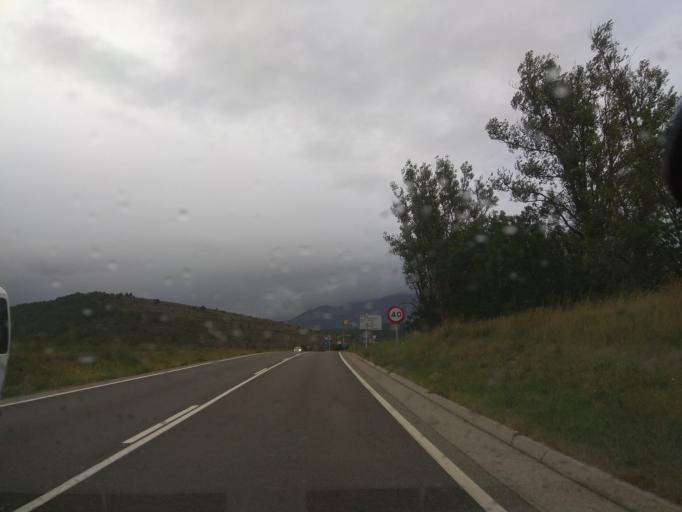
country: ES
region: Catalonia
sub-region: Provincia de Lleida
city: Bellver de Cerdanya
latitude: 42.3674
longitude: 1.7951
